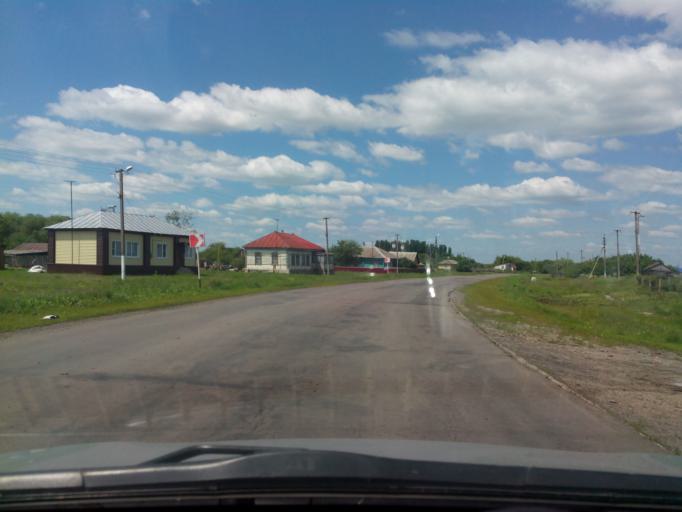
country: RU
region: Voronezj
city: Gribanovskiy
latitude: 51.6252
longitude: 41.9164
